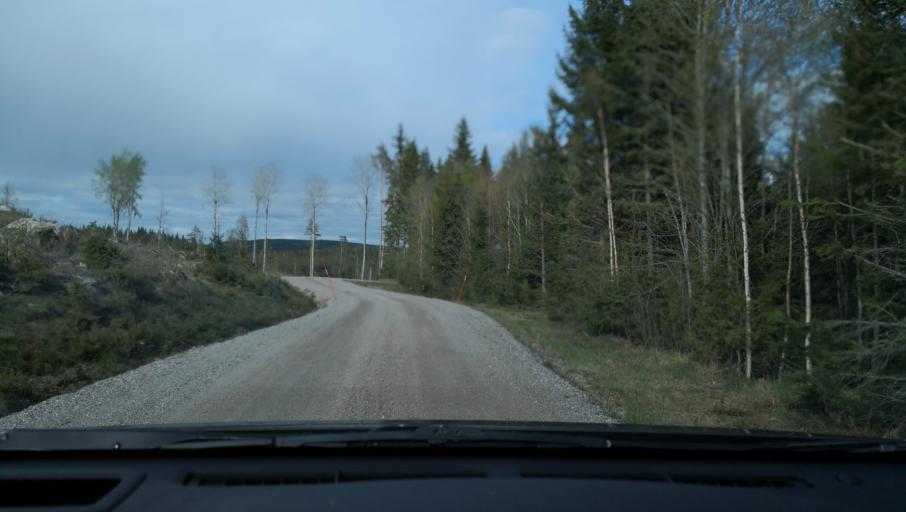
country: SE
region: Vaestmanland
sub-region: Fagersta Kommun
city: Fagersta
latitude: 60.1581
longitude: 15.7097
